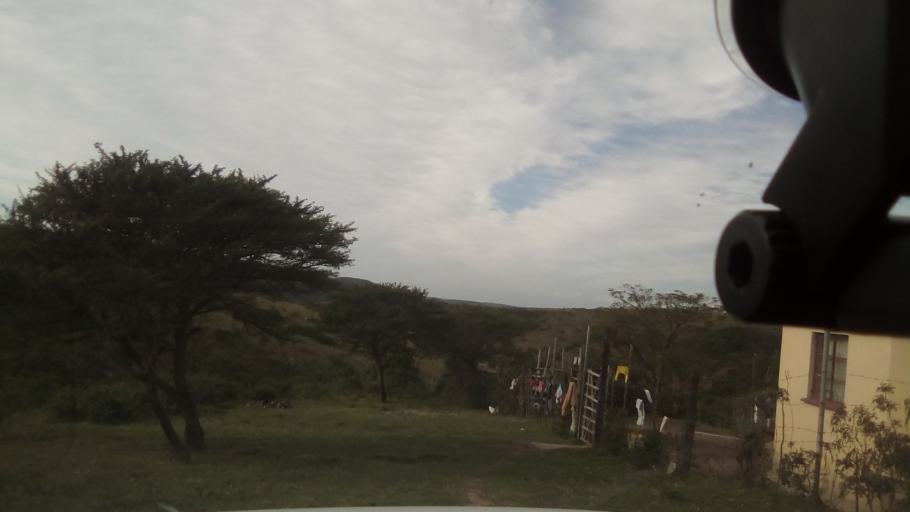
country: ZA
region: Eastern Cape
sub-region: Buffalo City Metropolitan Municipality
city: East London
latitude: -32.8010
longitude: 27.9679
